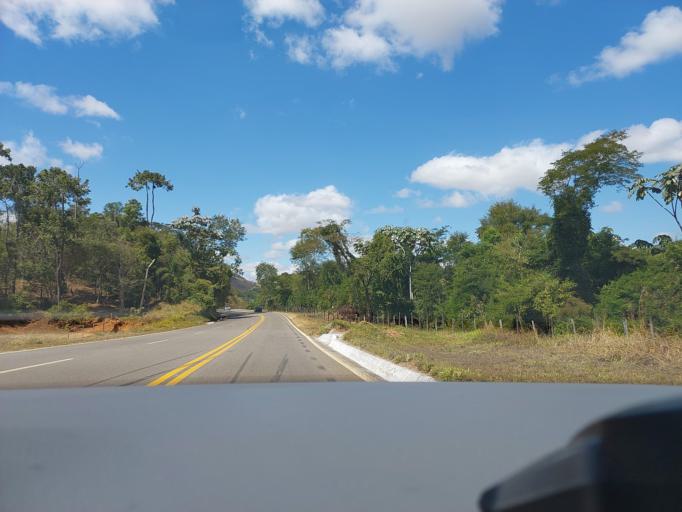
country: BR
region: Minas Gerais
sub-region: Mirai
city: Mirai
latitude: -21.0457
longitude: -42.5254
